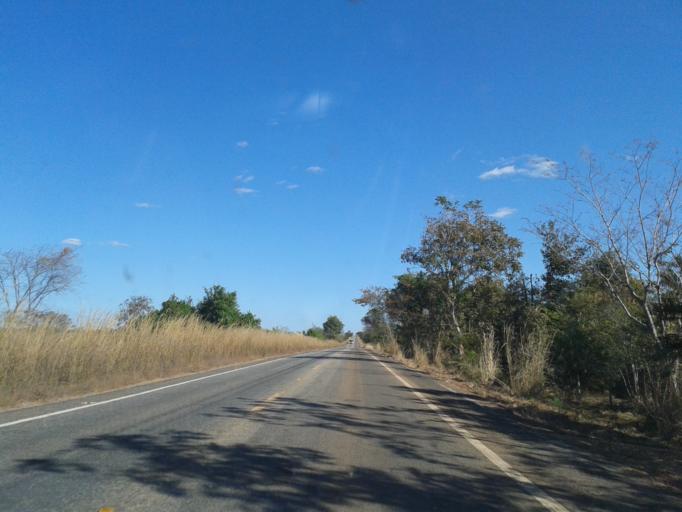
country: BR
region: Goias
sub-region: Mozarlandia
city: Mozarlandia
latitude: -14.5044
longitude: -50.4848
